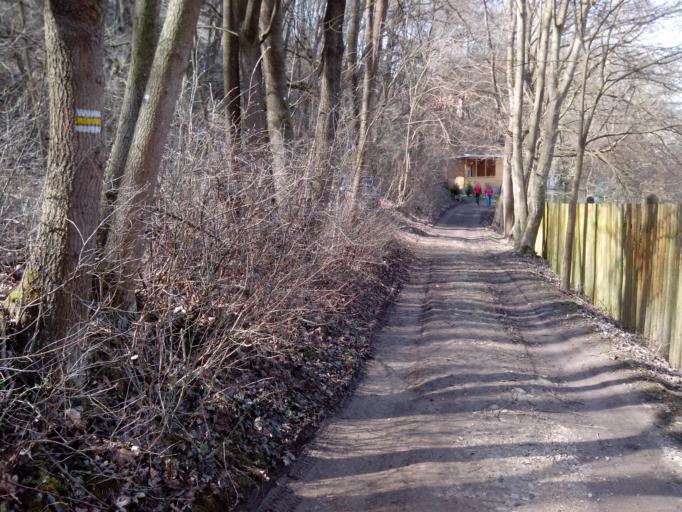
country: CZ
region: Central Bohemia
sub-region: Okres Beroun
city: Beroun
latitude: 49.9311
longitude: 14.1175
